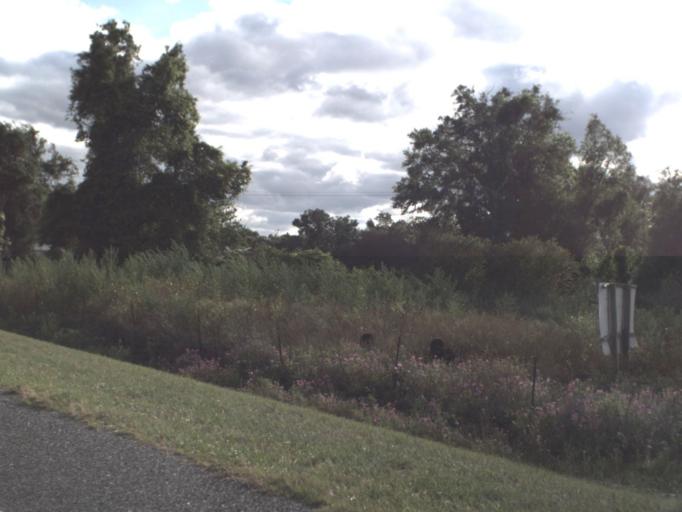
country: US
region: Florida
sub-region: Marion County
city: Citra
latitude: 29.4066
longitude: -82.1135
